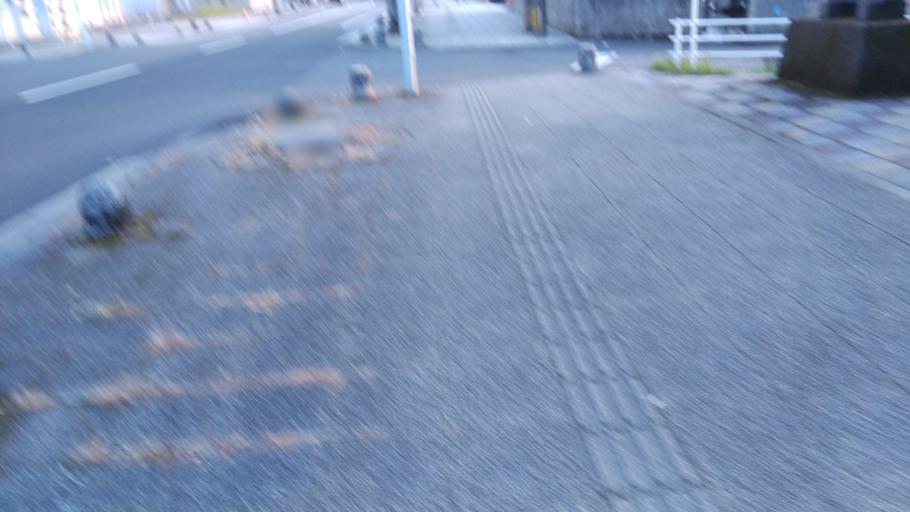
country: JP
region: Kagoshima
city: Kokubu-matsuki
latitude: 31.7424
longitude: 130.7635
